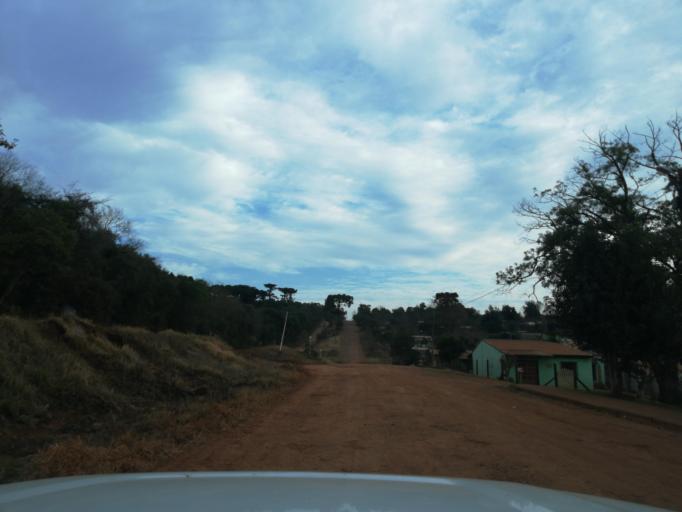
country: AR
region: Misiones
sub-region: Departamento de San Pedro
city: San Pedro
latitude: -26.6291
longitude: -54.0933
